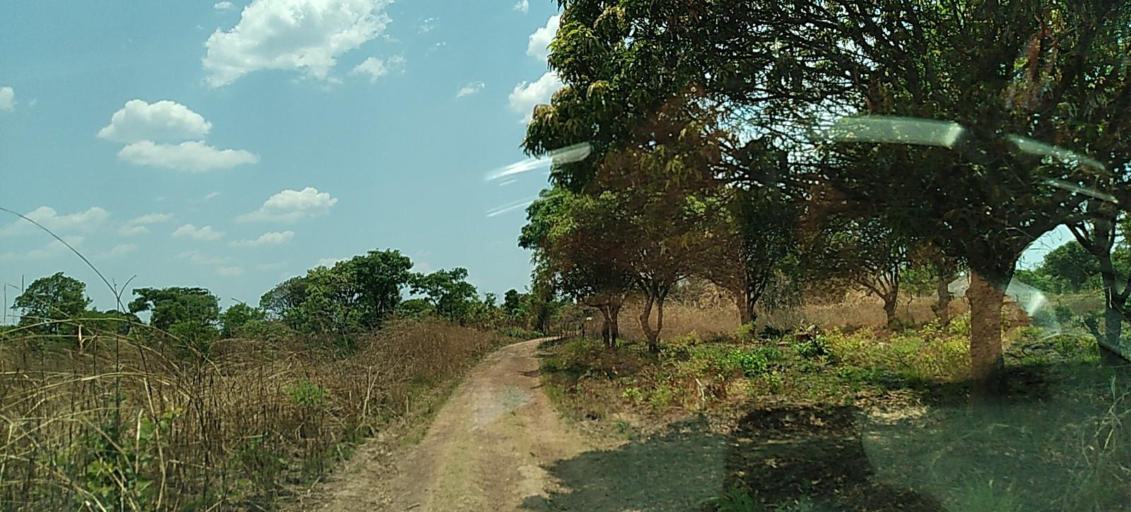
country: ZM
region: Copperbelt
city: Chililabombwe
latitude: -12.4667
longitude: 27.6670
